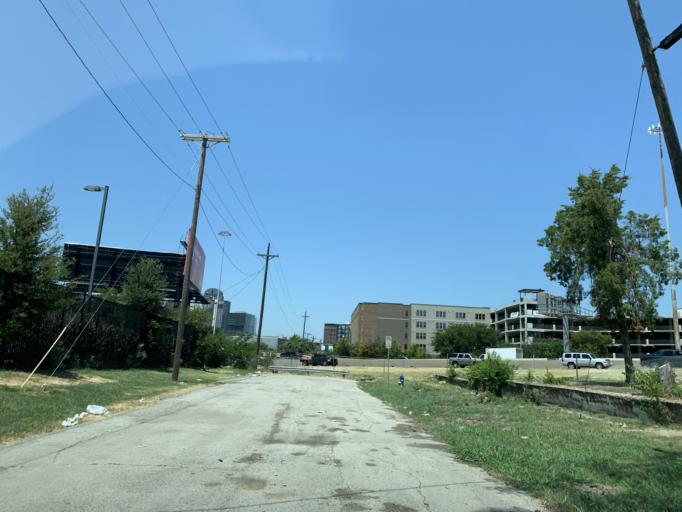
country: US
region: Texas
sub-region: Dallas County
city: Dallas
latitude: 32.7796
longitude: -96.7779
